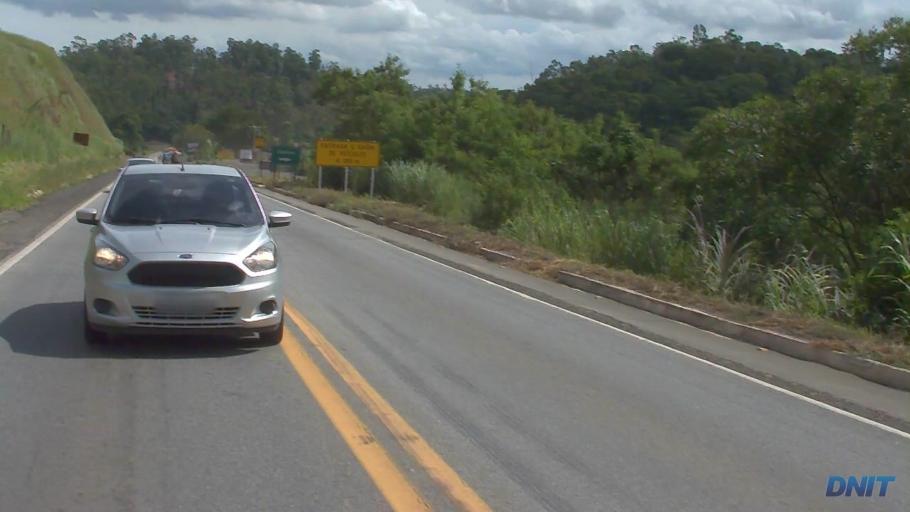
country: BR
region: Minas Gerais
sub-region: Ipatinga
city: Ipatinga
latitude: -19.4211
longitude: -42.4946
